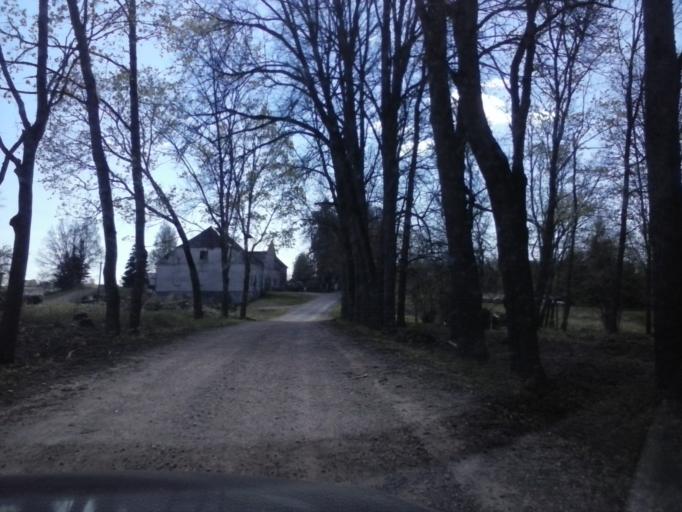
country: EE
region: Valgamaa
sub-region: Torva linn
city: Torva
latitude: 58.2327
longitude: 25.8911
